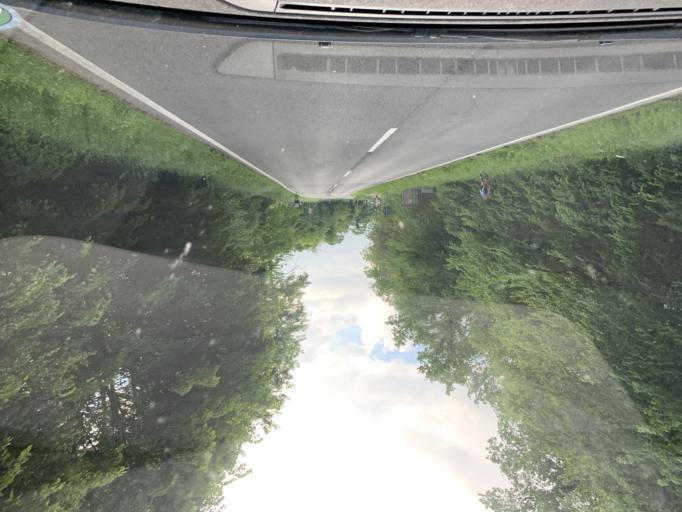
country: DE
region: North Rhine-Westphalia
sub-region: Regierungsbezirk Koln
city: Weilerswist
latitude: 50.7734
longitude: 6.8511
